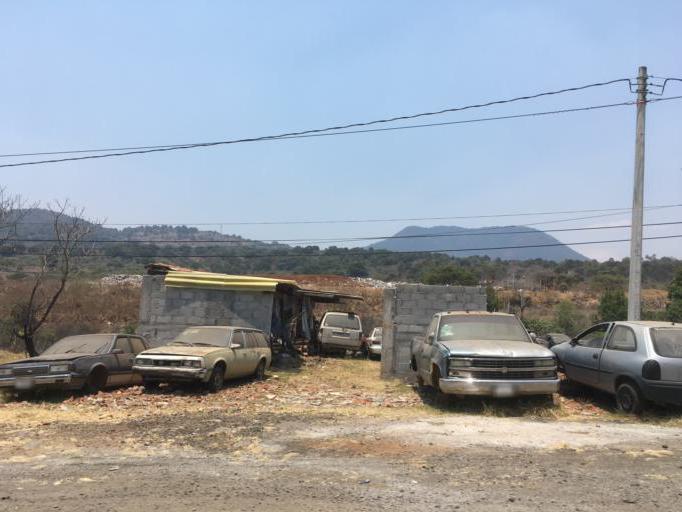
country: MX
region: Michoacan
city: Quiroga
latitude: 19.6581
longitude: -101.5075
